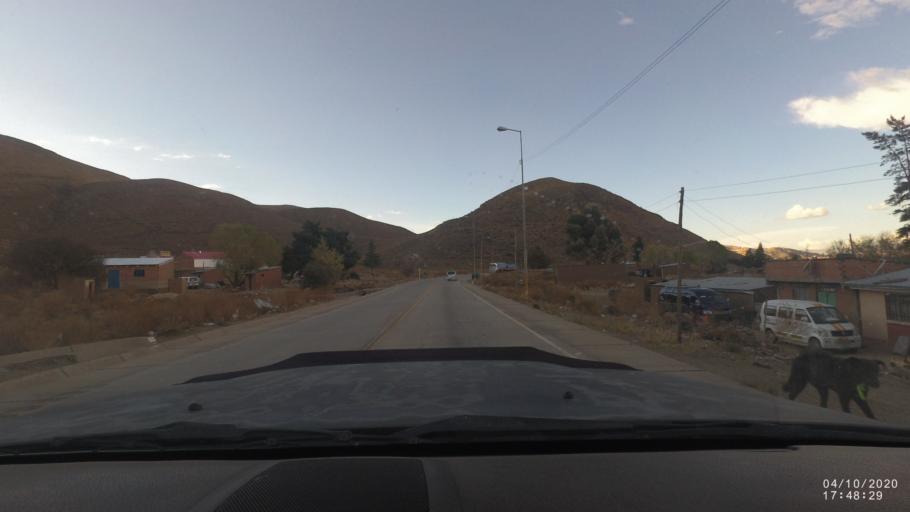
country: BO
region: Oruro
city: Oruro
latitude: -18.0167
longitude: -67.1394
